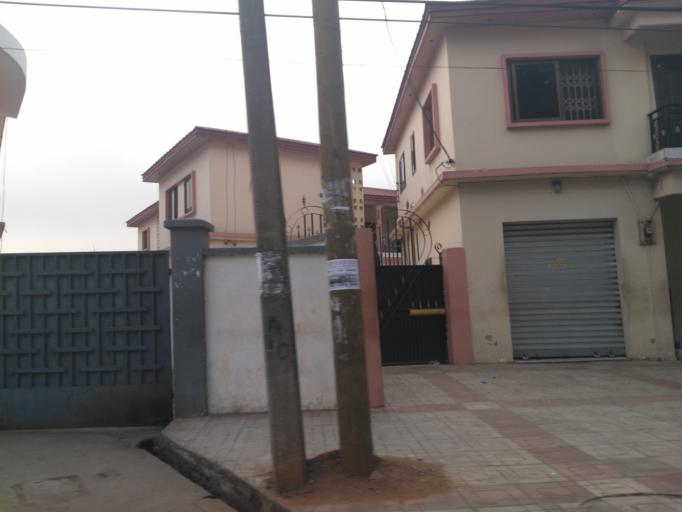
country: GH
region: Ashanti
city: Kumasi
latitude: 6.7026
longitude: -1.6154
